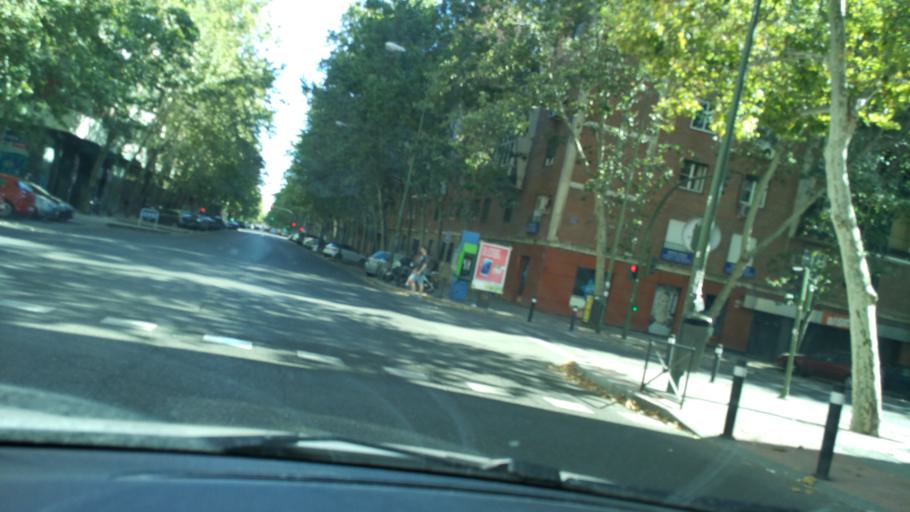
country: ES
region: Madrid
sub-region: Provincia de Madrid
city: Chamartin
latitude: 40.4579
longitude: -3.6943
